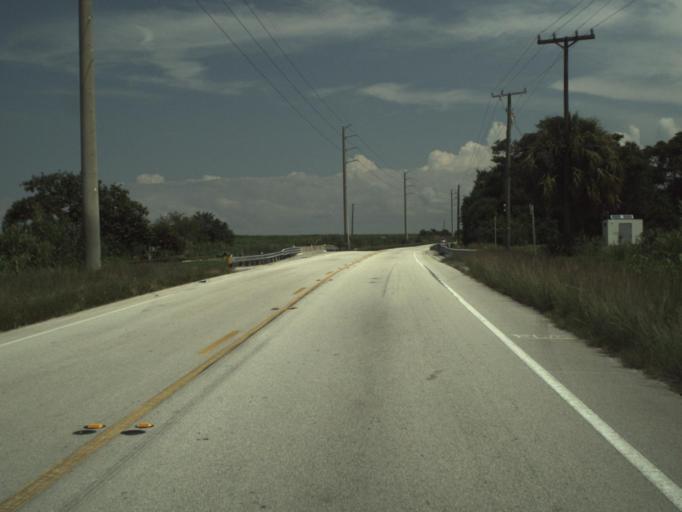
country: US
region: Florida
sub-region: Palm Beach County
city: Pahokee
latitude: 26.9163
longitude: -80.6131
